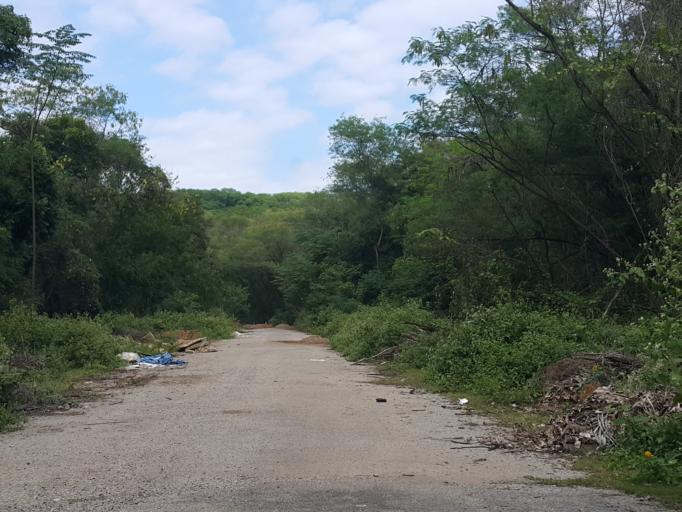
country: TH
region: Lampang
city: Mae Mo
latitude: 18.3254
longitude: 99.7526
